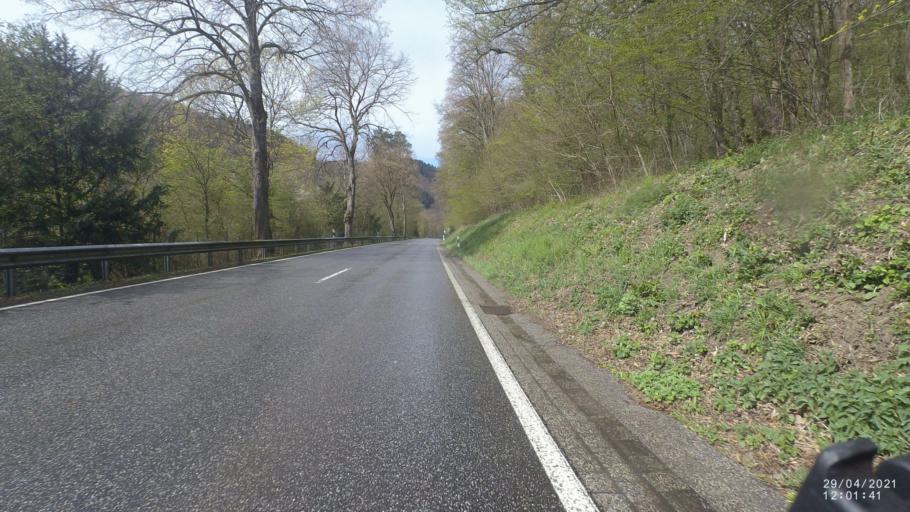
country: DE
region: Rheinland-Pfalz
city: Sankt Johann
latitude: 50.3438
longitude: 7.1959
